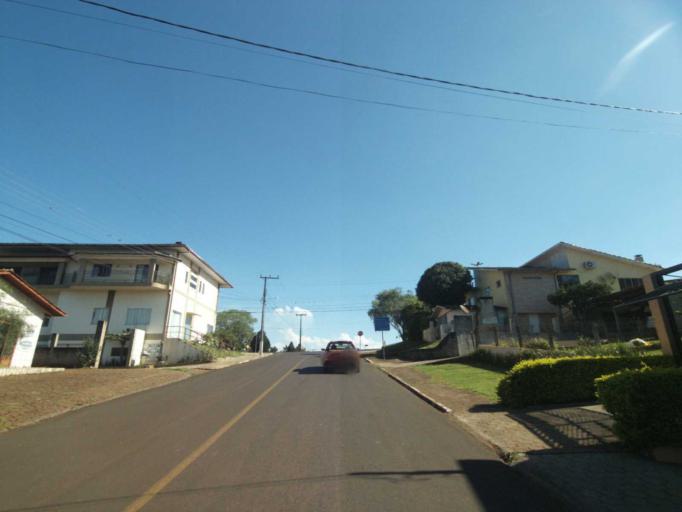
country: BR
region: Parana
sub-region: Laranjeiras Do Sul
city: Laranjeiras do Sul
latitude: -25.3811
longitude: -52.2023
